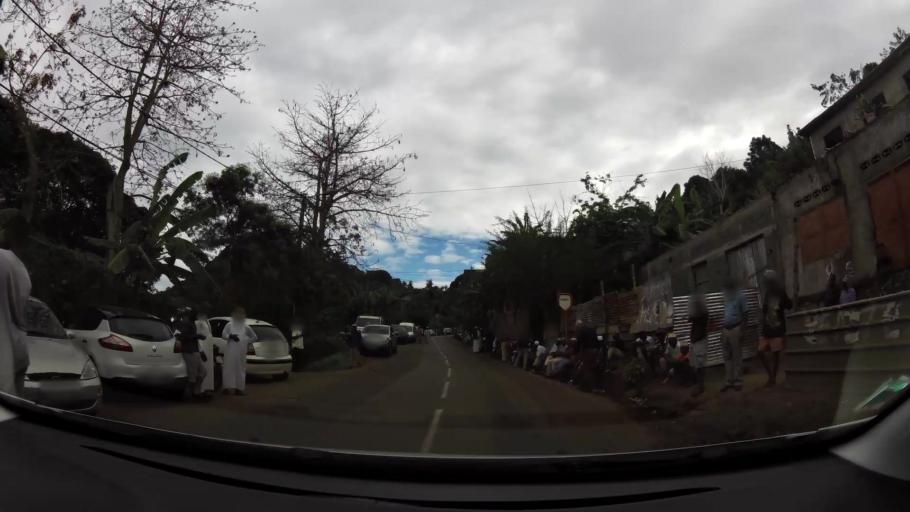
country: YT
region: Chiconi
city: Chiconi
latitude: -12.8355
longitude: 45.1146
